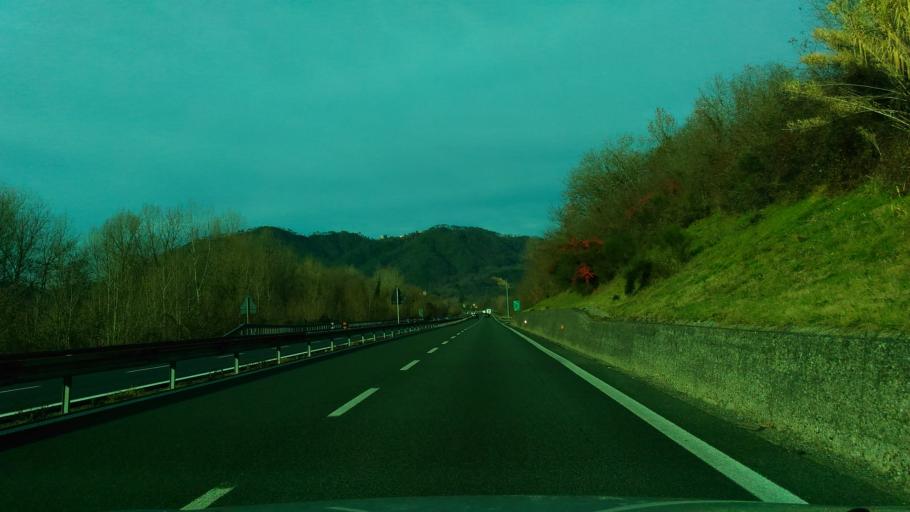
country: IT
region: Liguria
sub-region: Provincia di La Spezia
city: Beverino
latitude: 44.2008
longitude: 9.8072
